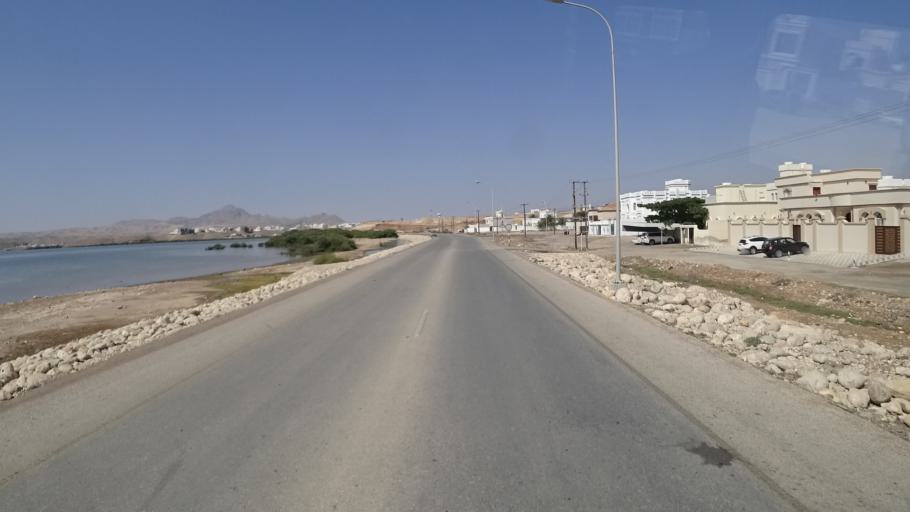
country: OM
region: Ash Sharqiyah
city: Sur
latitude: 22.5687
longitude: 59.5132
